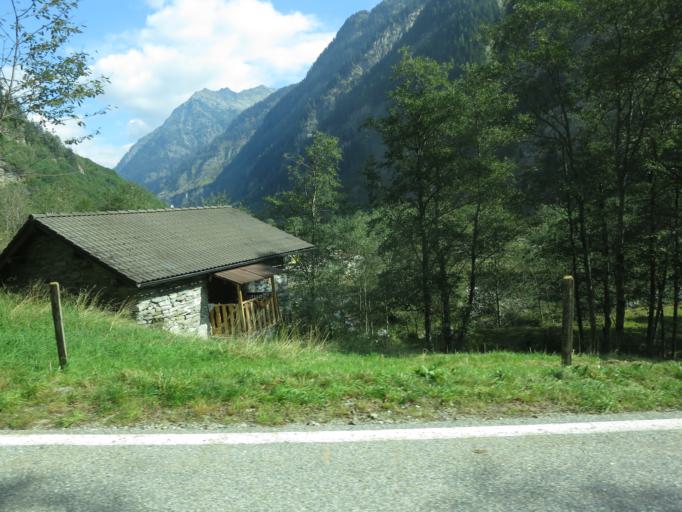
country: CH
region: Grisons
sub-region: Moesa District
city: Cauco
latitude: 46.3429
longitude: 9.1184
